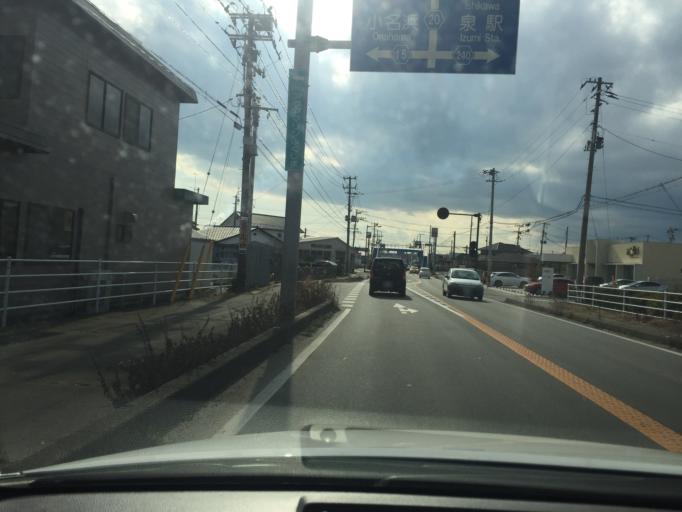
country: JP
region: Fukushima
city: Iwaki
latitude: 36.9551
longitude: 140.8671
